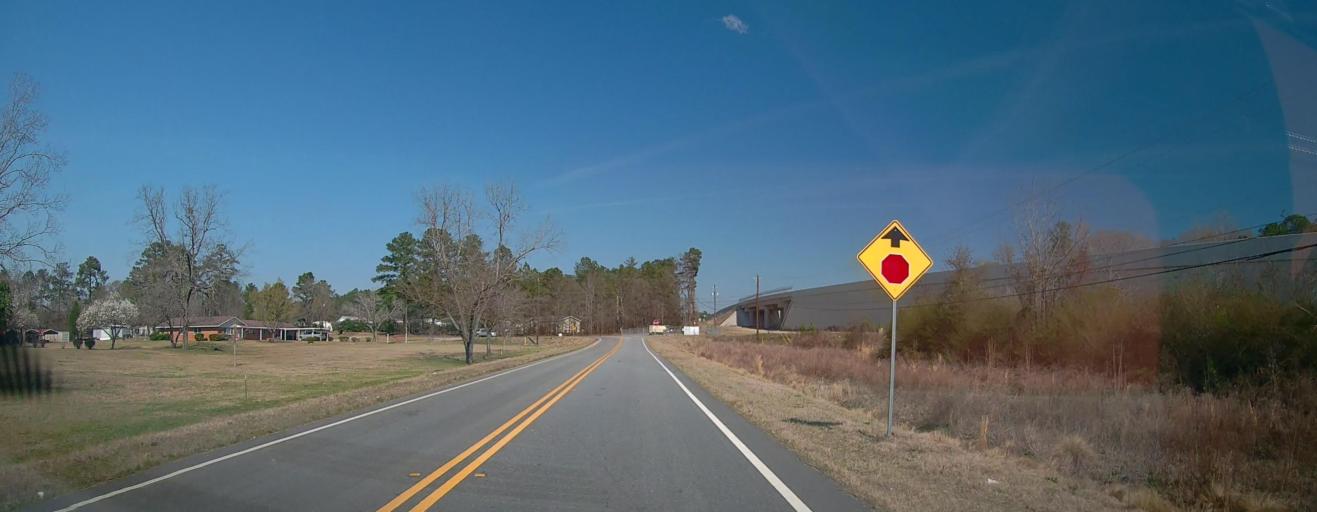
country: US
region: Georgia
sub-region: Bibb County
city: Macon
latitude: 32.8847
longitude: -83.5428
